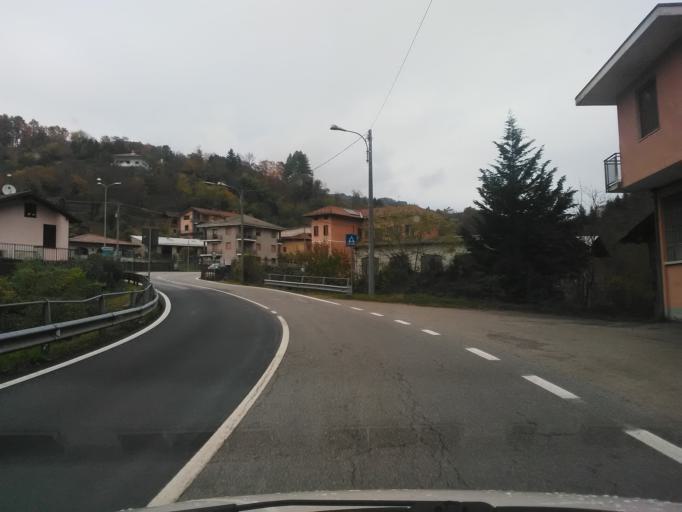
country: IT
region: Piedmont
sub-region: Provincia di Vercelli
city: Valduggia
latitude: 45.7310
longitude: 8.3344
